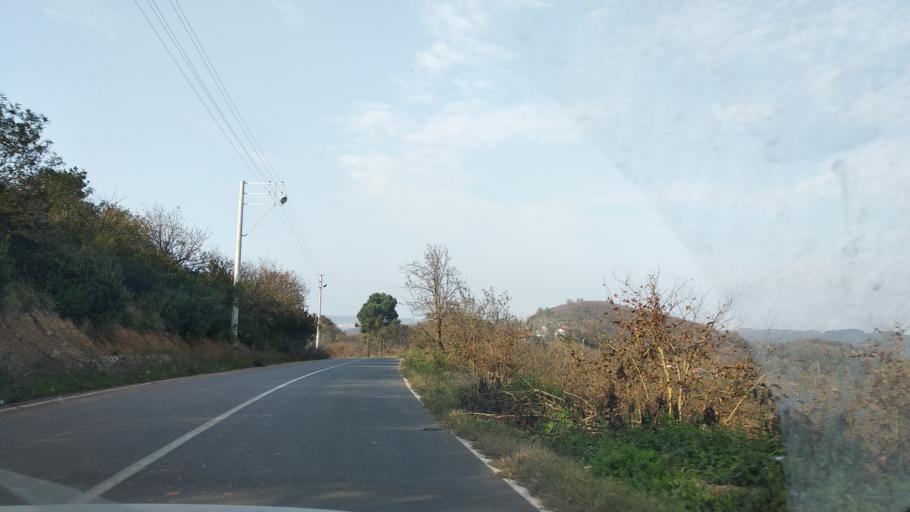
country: TR
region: Sakarya
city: Karasu
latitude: 41.0686
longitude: 30.6149
